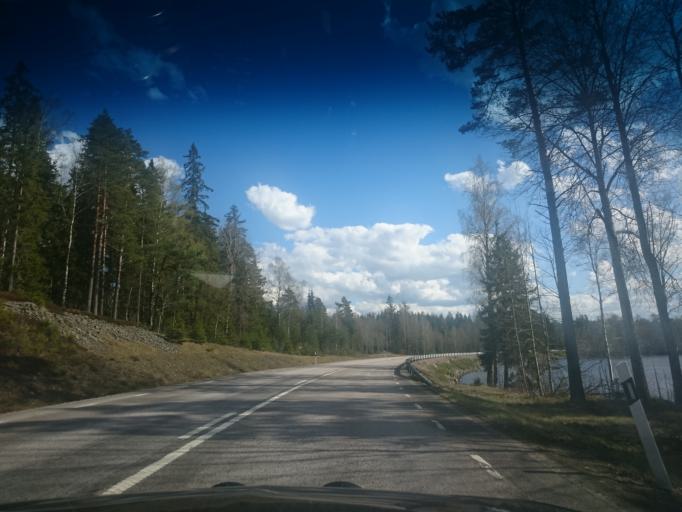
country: SE
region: Kronoberg
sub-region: Vaxjo Kommun
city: Braas
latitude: 57.2347
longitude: 15.1472
